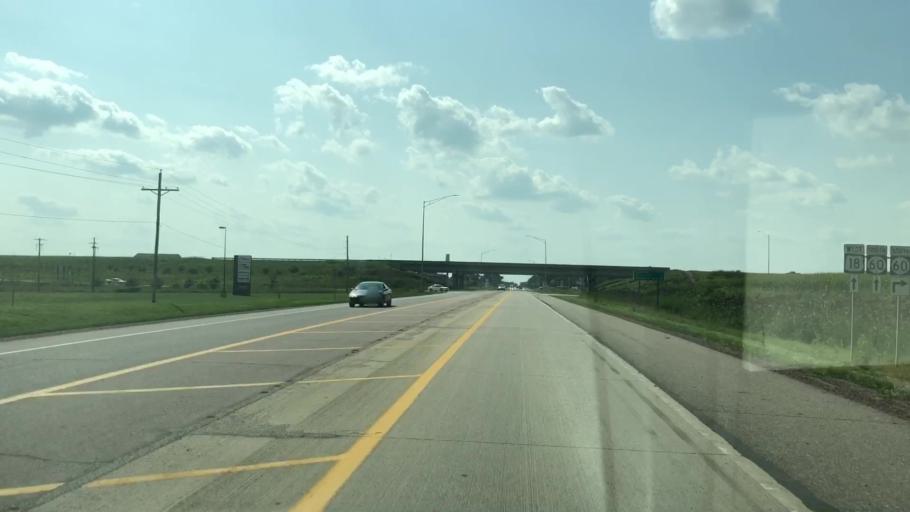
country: US
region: Iowa
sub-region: O'Brien County
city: Sheldon
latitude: 43.1861
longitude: -95.8096
